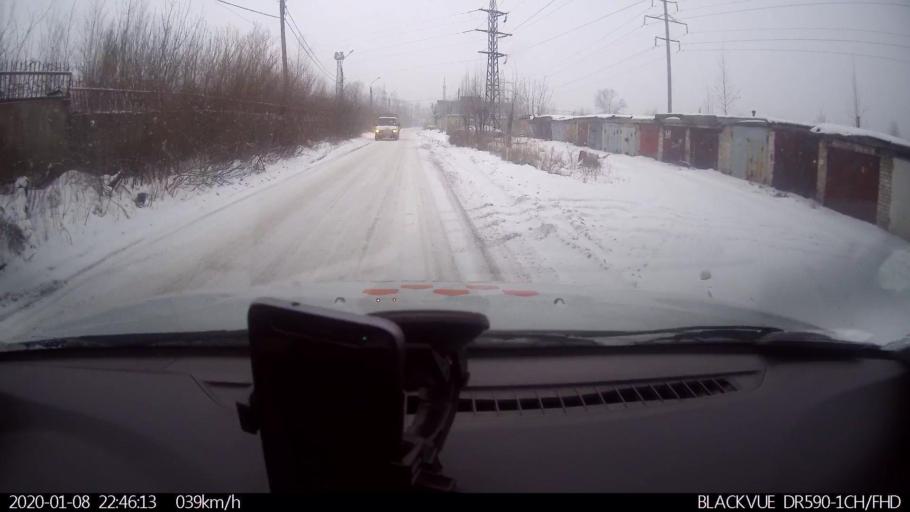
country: RU
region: Nizjnij Novgorod
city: Nizhniy Novgorod
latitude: 56.2968
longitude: 43.8955
